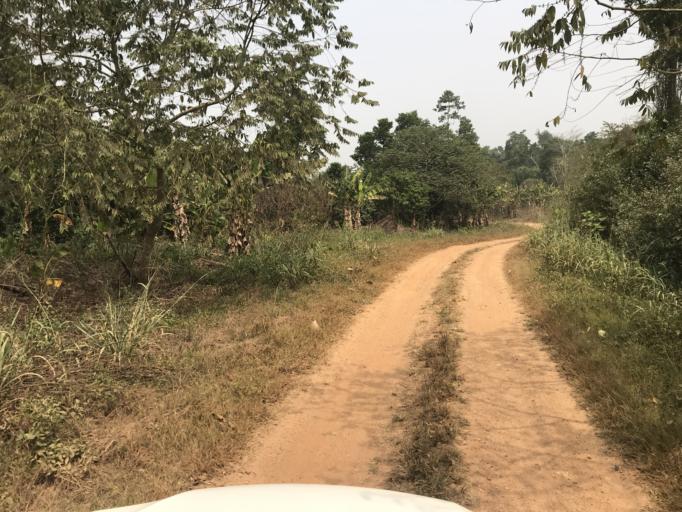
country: NG
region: Osun
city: Ifetedo
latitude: 7.0336
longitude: 4.4526
